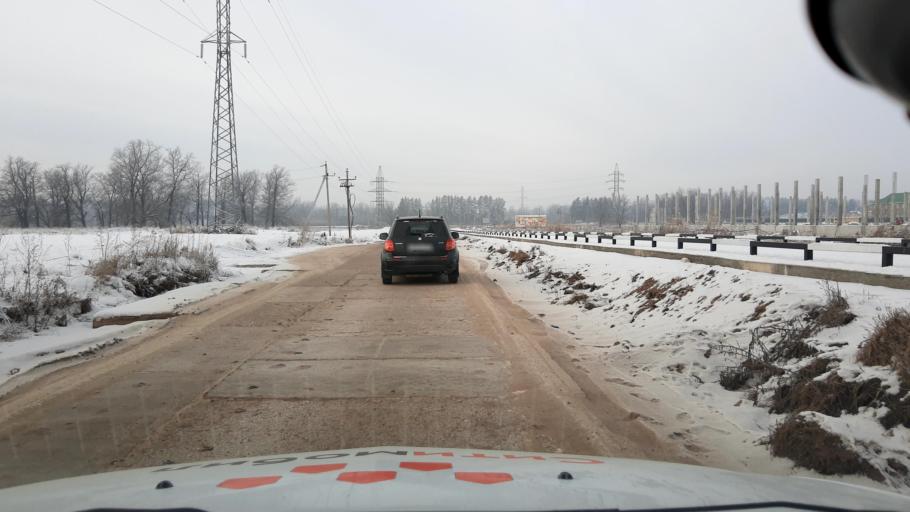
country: RU
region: Bashkortostan
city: Ufa
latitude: 54.7794
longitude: 55.9545
